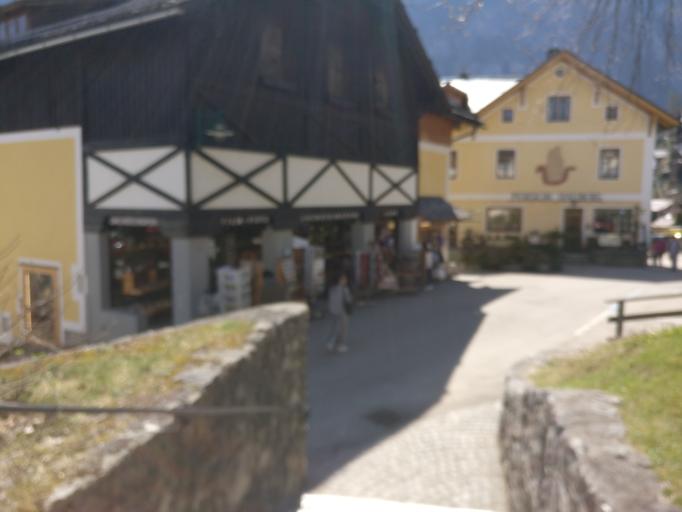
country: AT
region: Upper Austria
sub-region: Politischer Bezirk Gmunden
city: Bad Goisern
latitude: 47.5616
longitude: 13.6490
